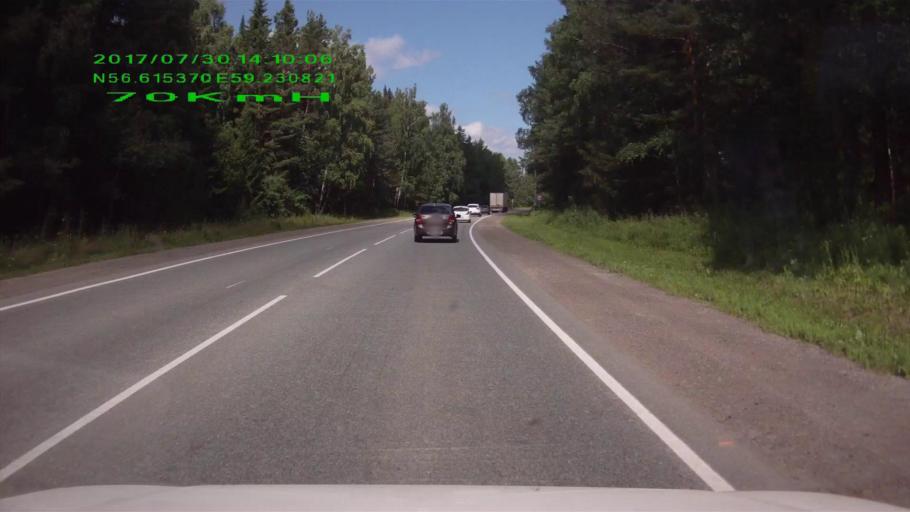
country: RU
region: Sverdlovsk
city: Nizhniye Sergi
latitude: 56.6156
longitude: 59.2309
